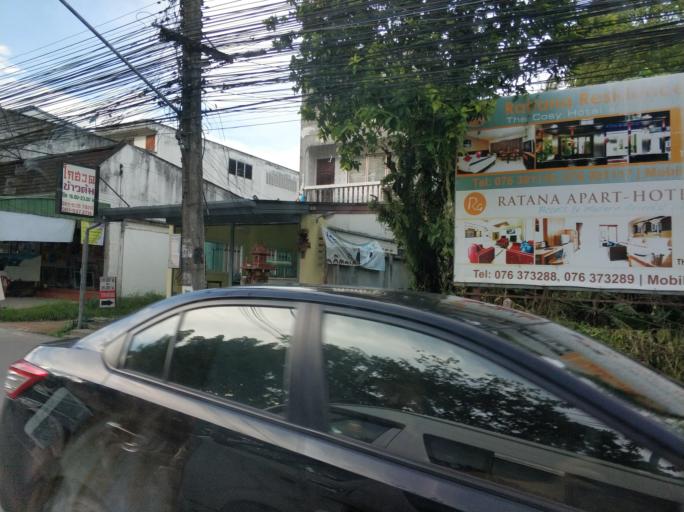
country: TH
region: Phuket
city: Wichit
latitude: 7.8875
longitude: 98.3726
